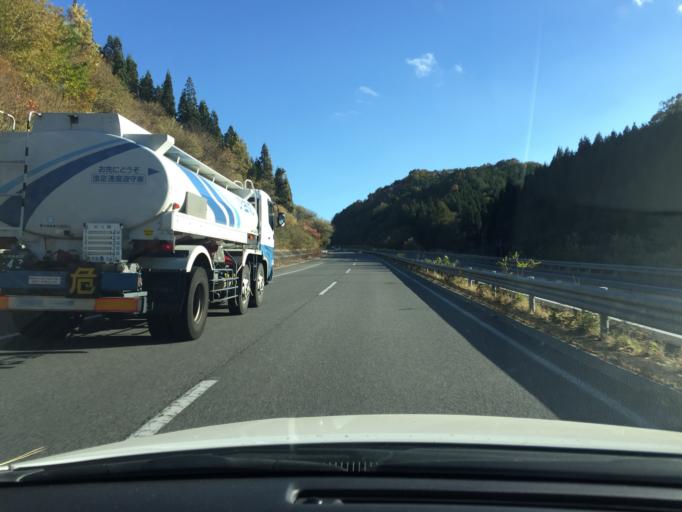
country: JP
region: Fukushima
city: Funehikimachi-funehiki
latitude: 37.2357
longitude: 140.6783
